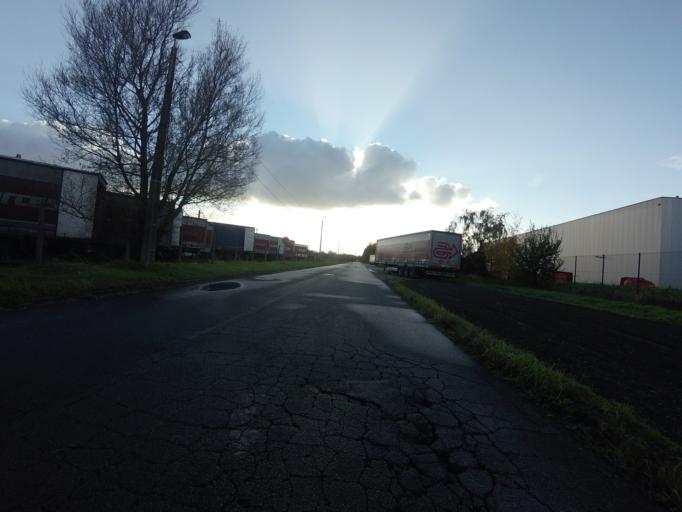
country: BE
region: Flanders
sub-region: Provincie Antwerpen
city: Boom
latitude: 51.0938
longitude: 4.3629
